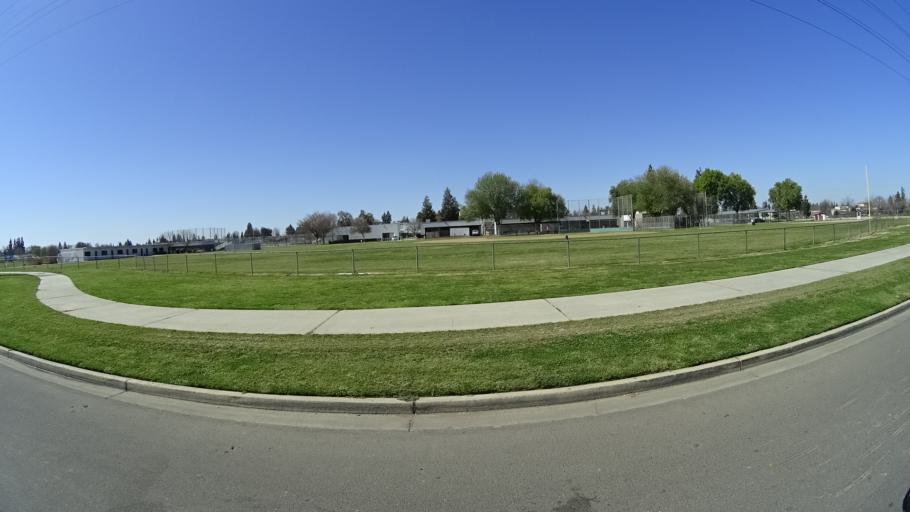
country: US
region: California
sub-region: Fresno County
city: Clovis
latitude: 36.8486
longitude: -119.7697
